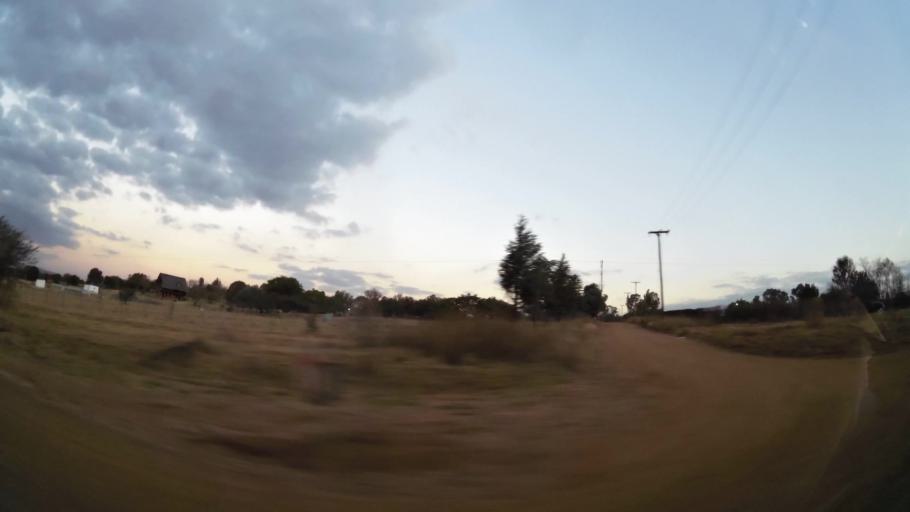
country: ZA
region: Gauteng
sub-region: West Rand District Municipality
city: Krugersdorp
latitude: -26.0678
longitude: 27.6881
